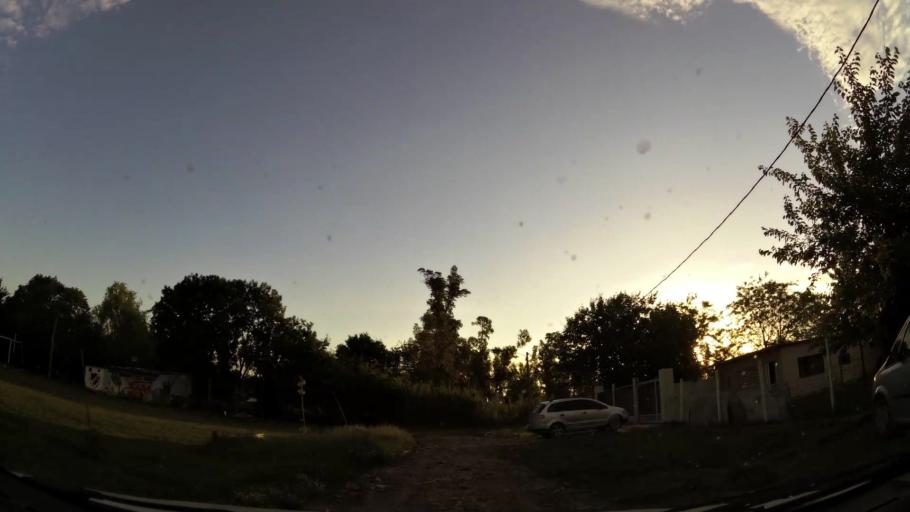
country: AR
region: Buenos Aires
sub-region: Partido de Merlo
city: Merlo
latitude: -34.6705
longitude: -58.7775
